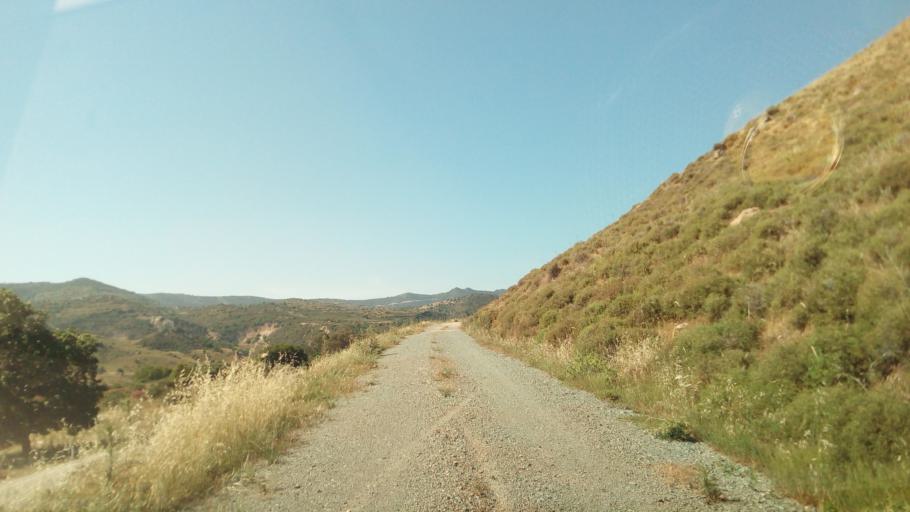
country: CY
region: Limassol
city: Pachna
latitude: 34.8121
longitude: 32.7142
